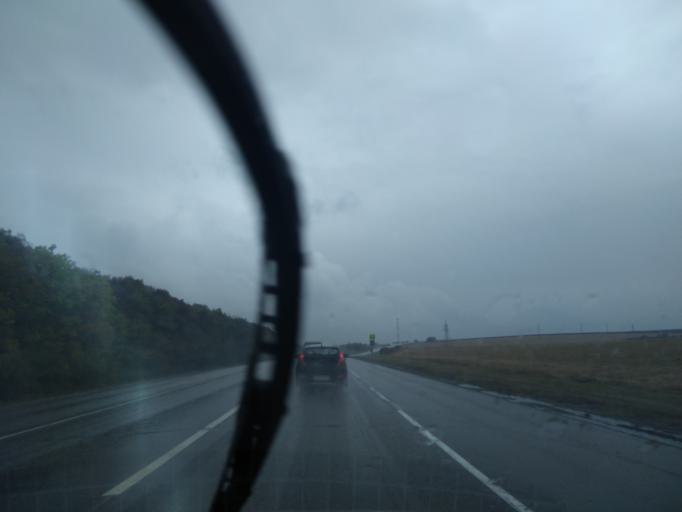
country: RU
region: Tula
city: Shchekino
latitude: 53.9645
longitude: 37.4823
